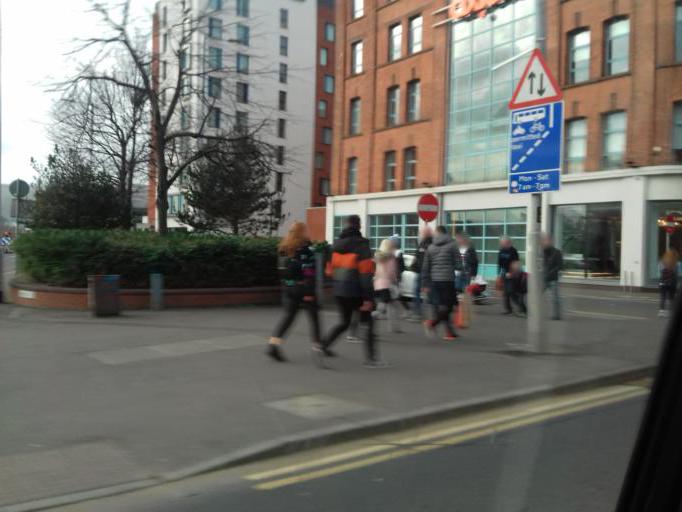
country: GB
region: Northern Ireland
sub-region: City of Belfast
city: Belfast
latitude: 54.5932
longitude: -5.9342
